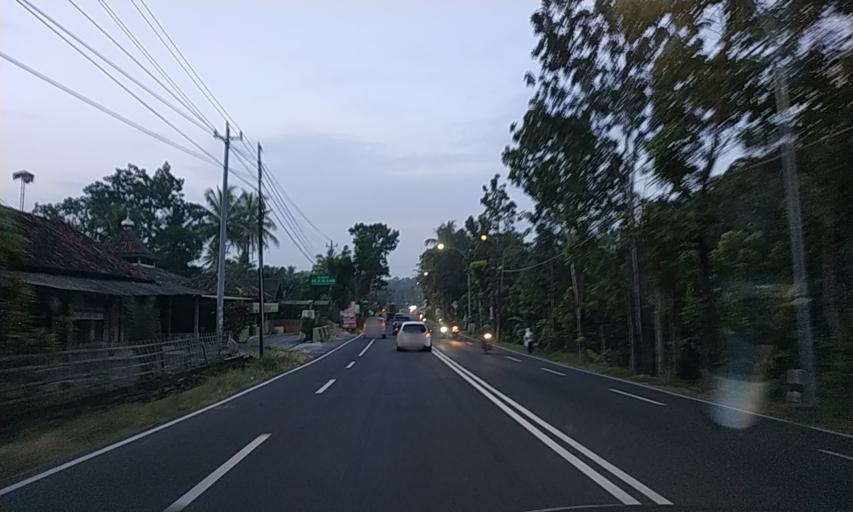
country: ID
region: Daerah Istimewa Yogyakarta
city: Srandakan
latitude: -7.8623
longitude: 110.2115
